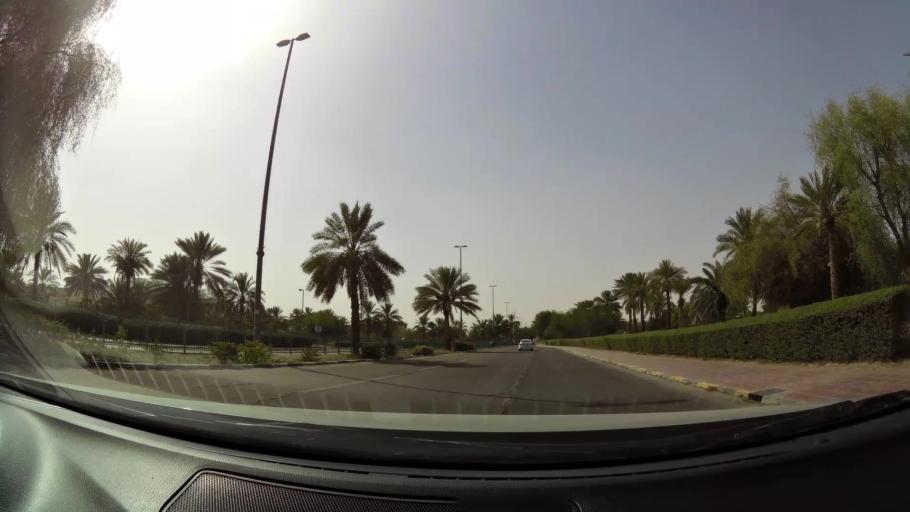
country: AE
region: Abu Dhabi
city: Al Ain
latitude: 24.2334
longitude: 55.6918
